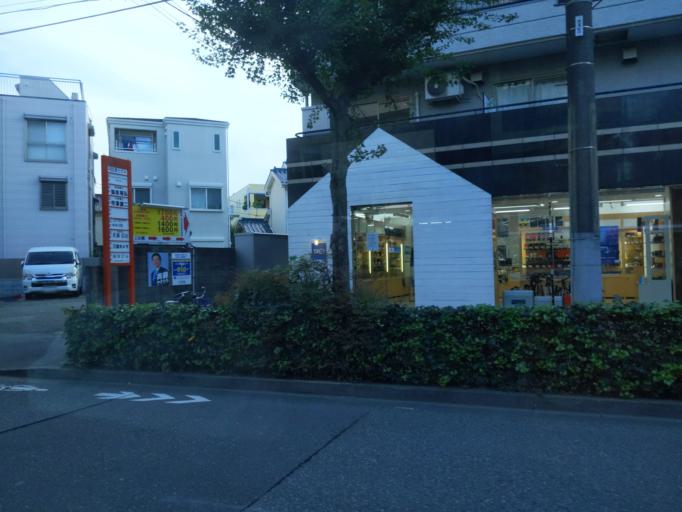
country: JP
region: Tokyo
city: Tokyo
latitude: 35.6264
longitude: 139.6940
